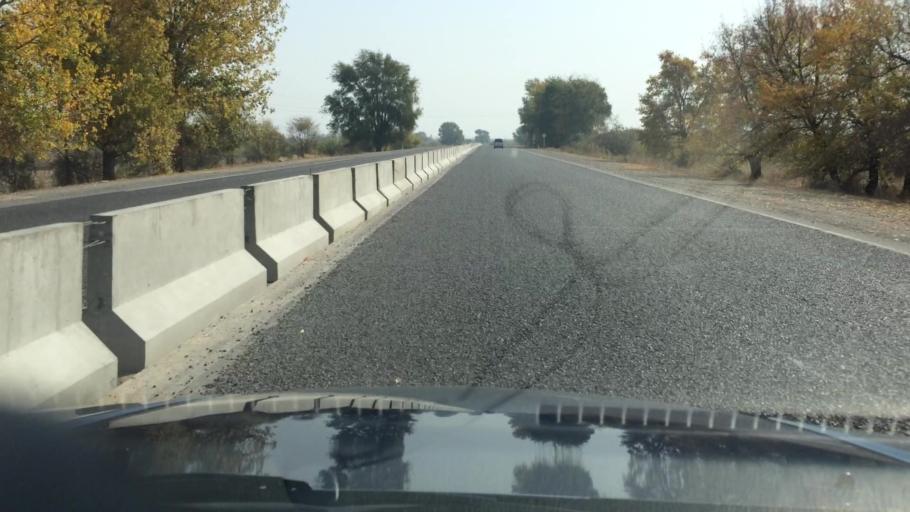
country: KG
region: Chuy
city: Kant
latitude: 42.9627
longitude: 74.9176
